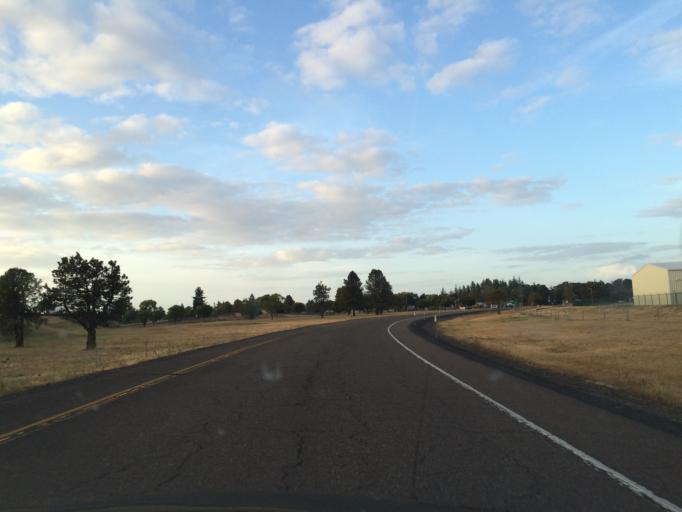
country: US
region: Oregon
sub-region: Linn County
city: Millersburg
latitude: 44.6413
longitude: -123.0620
